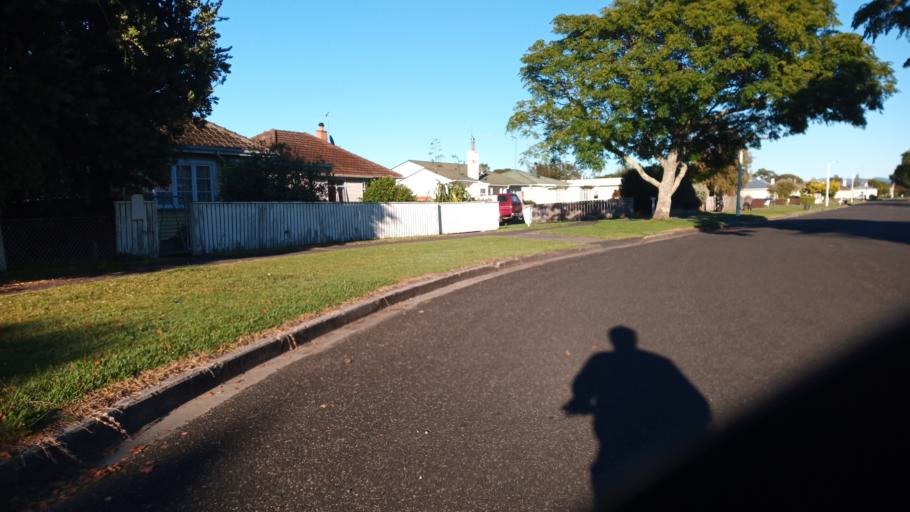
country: NZ
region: Gisborne
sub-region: Gisborne District
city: Gisborne
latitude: -38.6613
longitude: 178.0061
